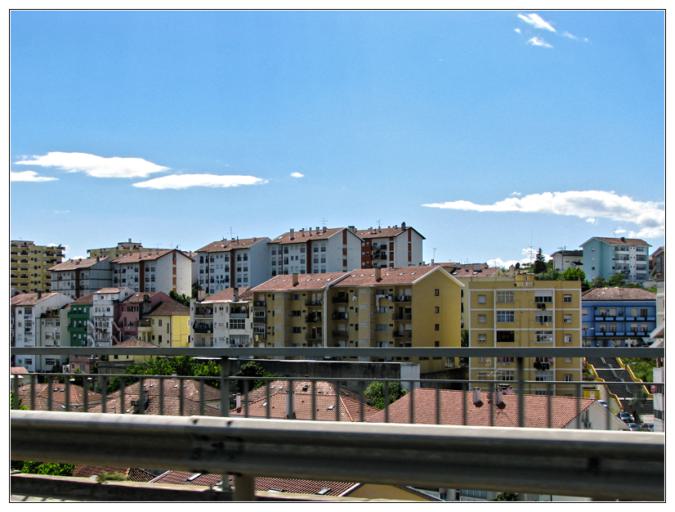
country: PT
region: Coimbra
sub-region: Coimbra
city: Coimbra
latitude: 40.2315
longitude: -8.4361
